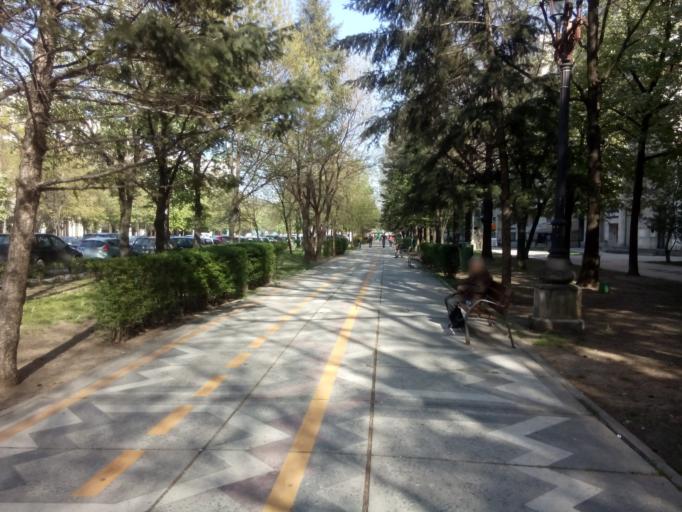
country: RO
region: Bucuresti
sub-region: Municipiul Bucuresti
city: Bucuresti
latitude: 44.4269
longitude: 26.0972
